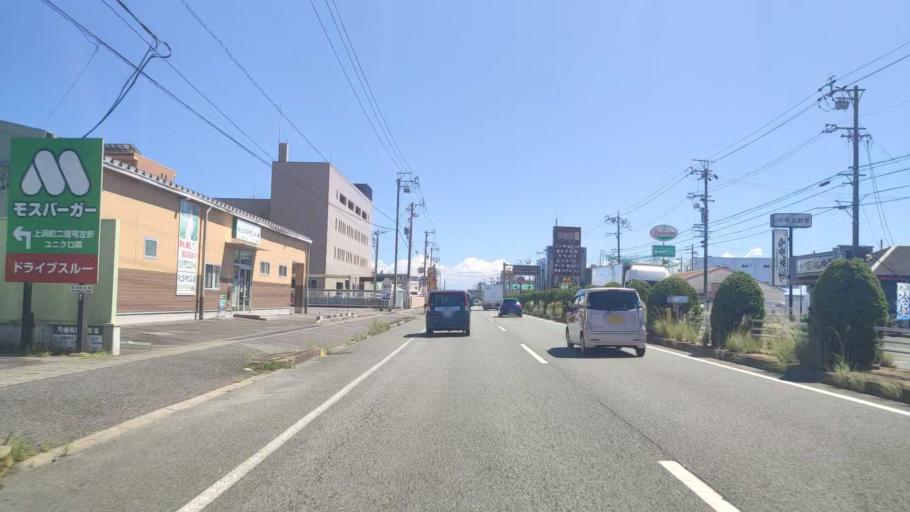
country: JP
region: Mie
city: Tsu-shi
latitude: 34.7516
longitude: 136.5219
